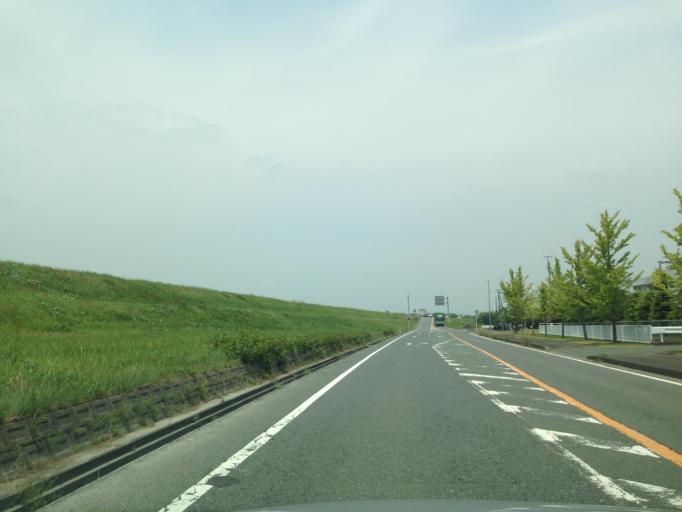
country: JP
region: Shizuoka
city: Hamakita
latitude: 34.7636
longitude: 137.8238
